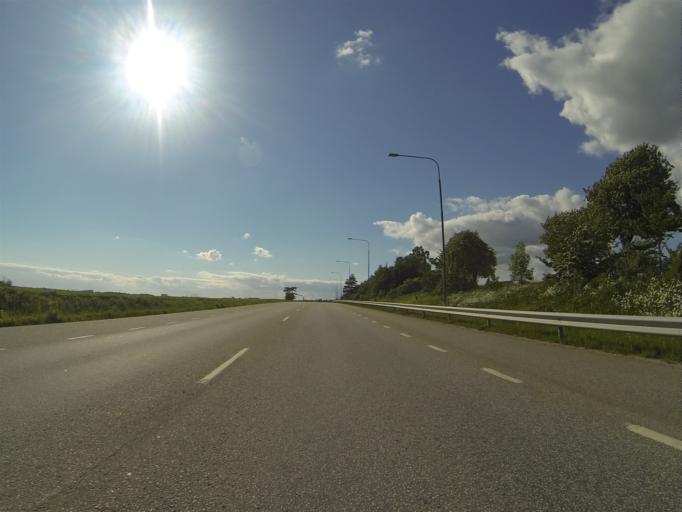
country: SE
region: Skane
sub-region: Lunds Kommun
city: Lund
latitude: 55.6882
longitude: 13.2547
